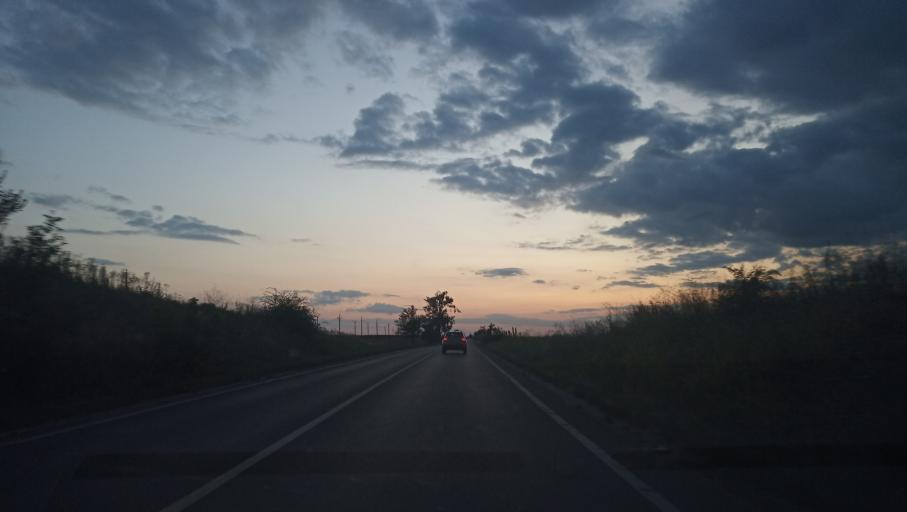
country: RO
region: Calarasi
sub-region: Comuna Tamadau Mare
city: Tamadau Mare
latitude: 44.4603
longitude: 26.5574
